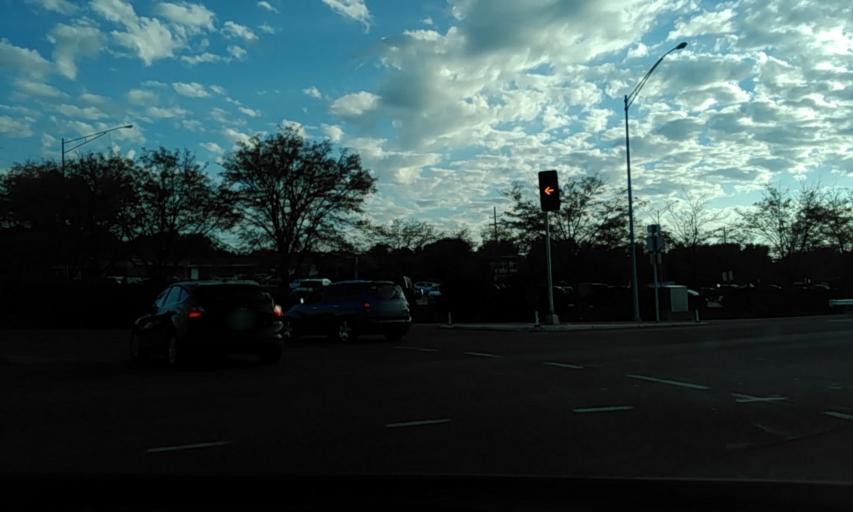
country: US
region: Missouri
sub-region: Saint Louis County
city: Sunset Hills
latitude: 38.5251
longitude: -90.3994
